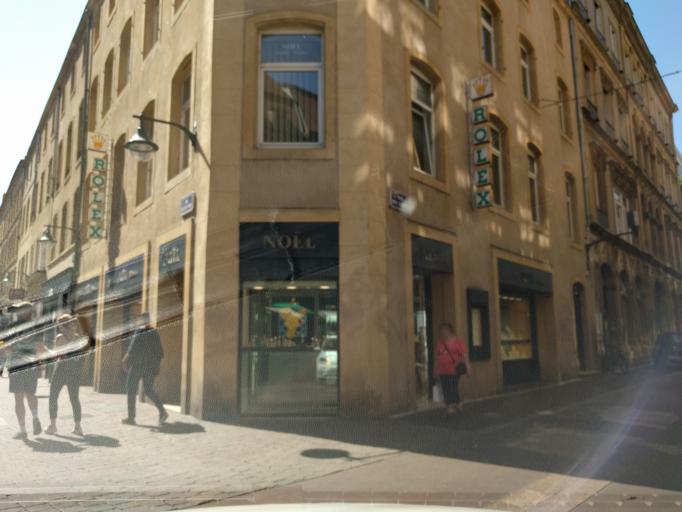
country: FR
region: Lorraine
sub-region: Departement de la Moselle
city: Metz
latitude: 49.1185
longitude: 6.1750
